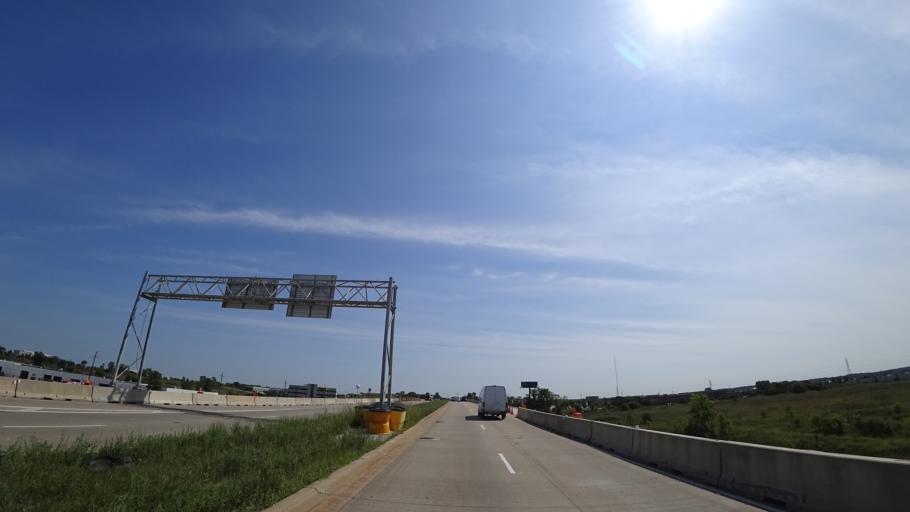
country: US
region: Illinois
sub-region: Cook County
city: Orland Hills
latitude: 41.5486
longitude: -87.8524
